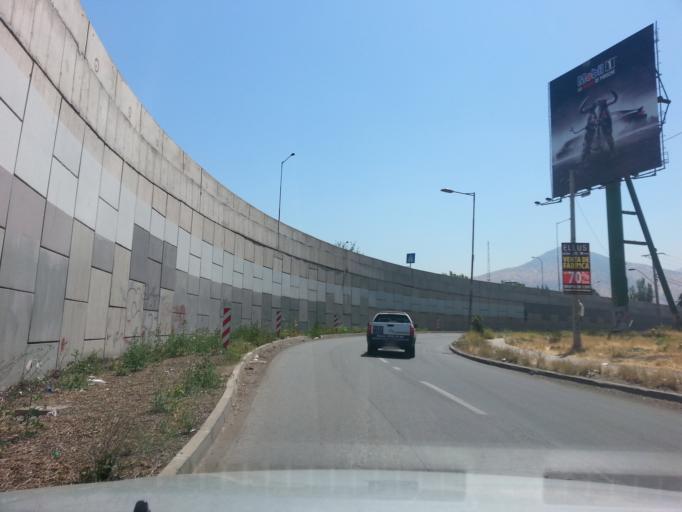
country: CL
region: Santiago Metropolitan
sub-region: Provincia de Santiago
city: Lo Prado
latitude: -33.3670
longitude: -70.6879
